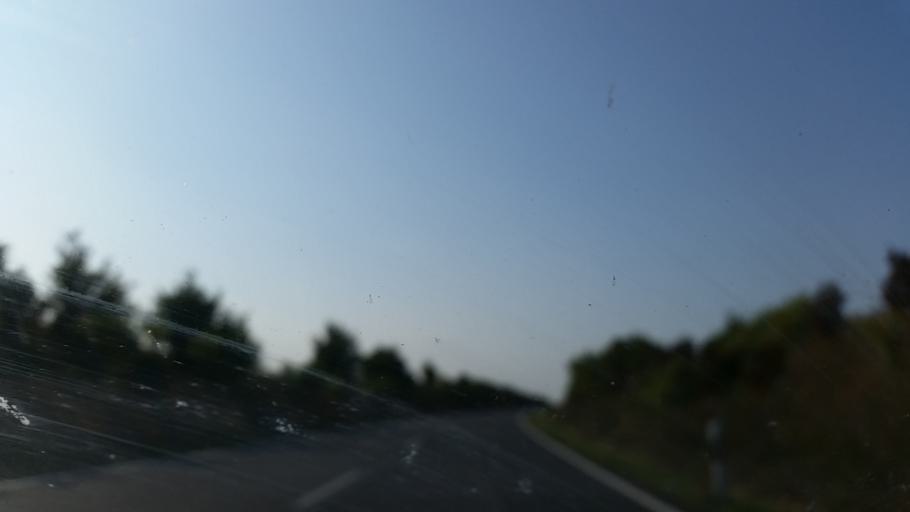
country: DE
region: Brandenburg
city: Zichow
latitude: 53.1987
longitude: 14.0336
